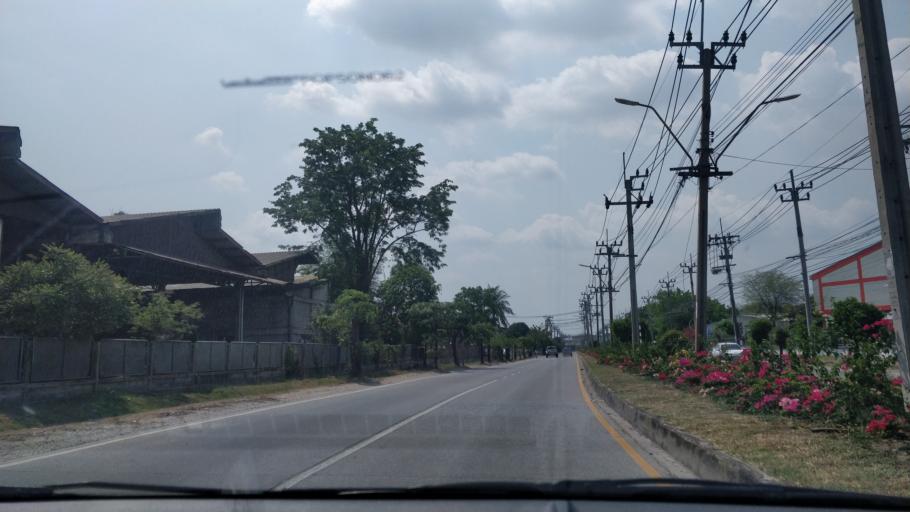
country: TH
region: Bangkok
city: Lat Krabang
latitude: 13.7580
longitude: 100.7879
